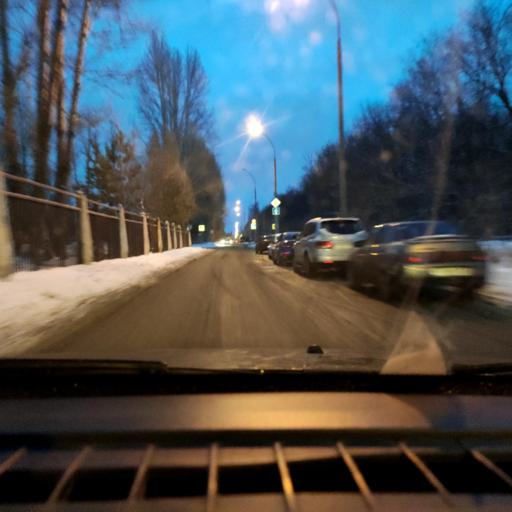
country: RU
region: Samara
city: Tol'yatti
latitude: 53.5025
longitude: 49.3037
